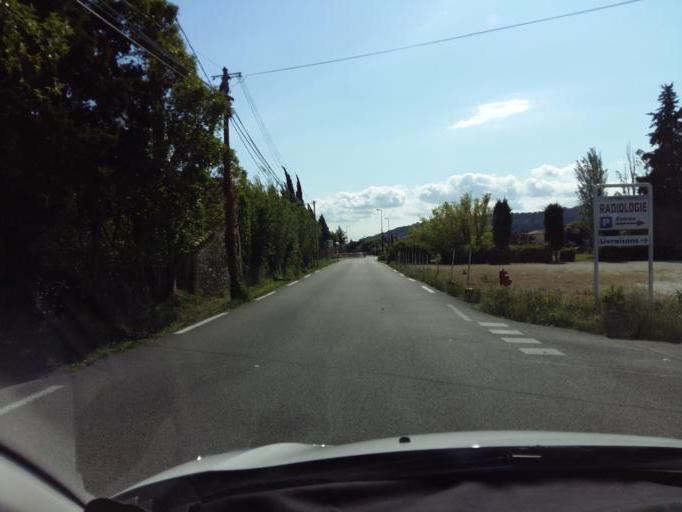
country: FR
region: Provence-Alpes-Cote d'Azur
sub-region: Departement du Vaucluse
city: Cavaillon
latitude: 43.8455
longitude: 5.0554
